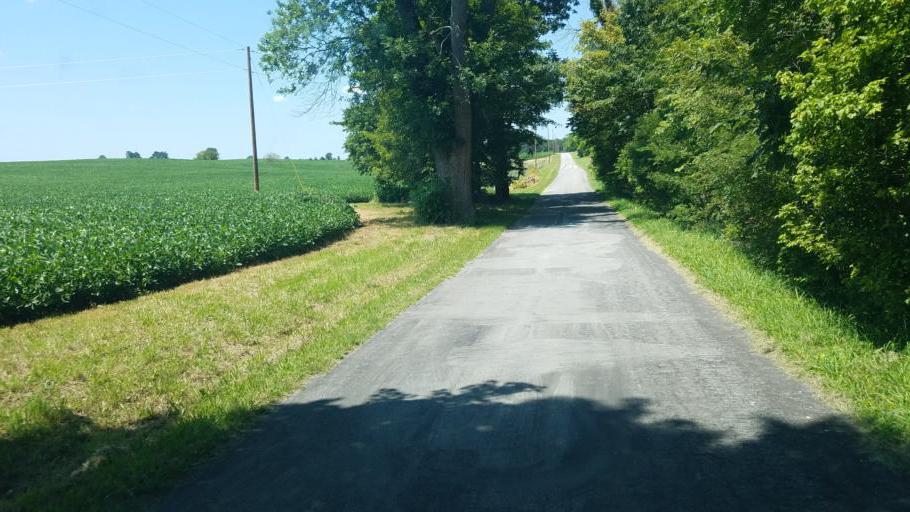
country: US
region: Ohio
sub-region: Marion County
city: Prospect
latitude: 40.5152
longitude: -83.2117
